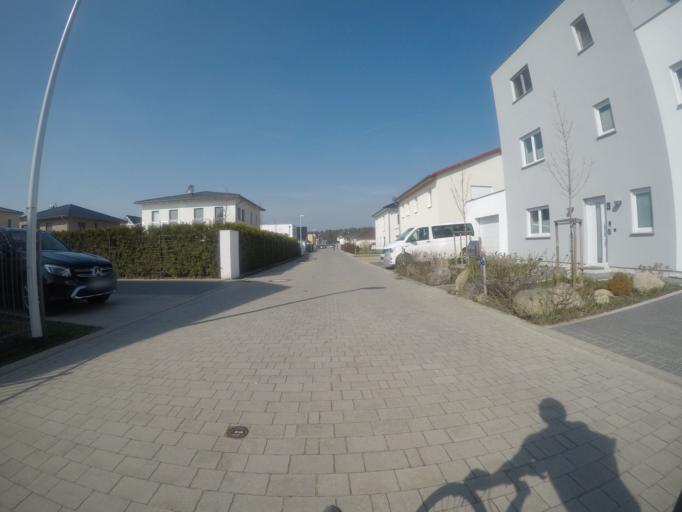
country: DE
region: Brandenburg
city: Konigs Wusterhausen
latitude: 52.2937
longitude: 13.6853
